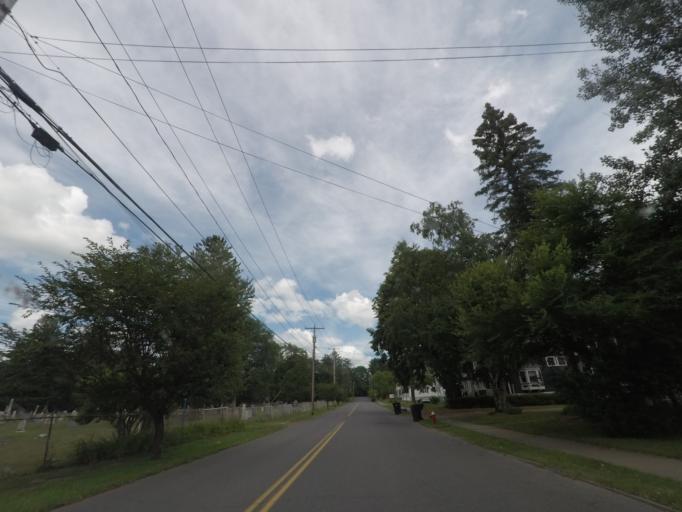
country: US
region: New York
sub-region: Rensselaer County
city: Troy
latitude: 42.7173
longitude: -73.6659
